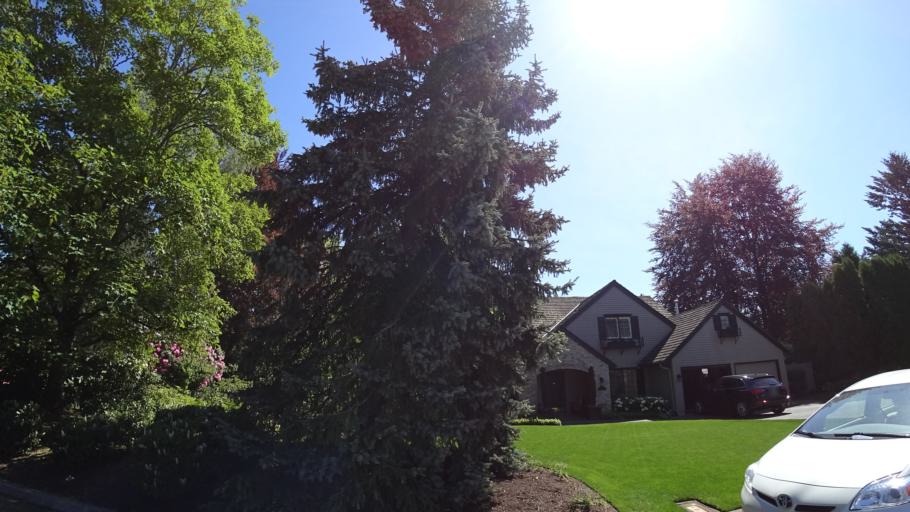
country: US
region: Oregon
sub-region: Washington County
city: Raleigh Hills
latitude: 45.4917
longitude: -122.7319
